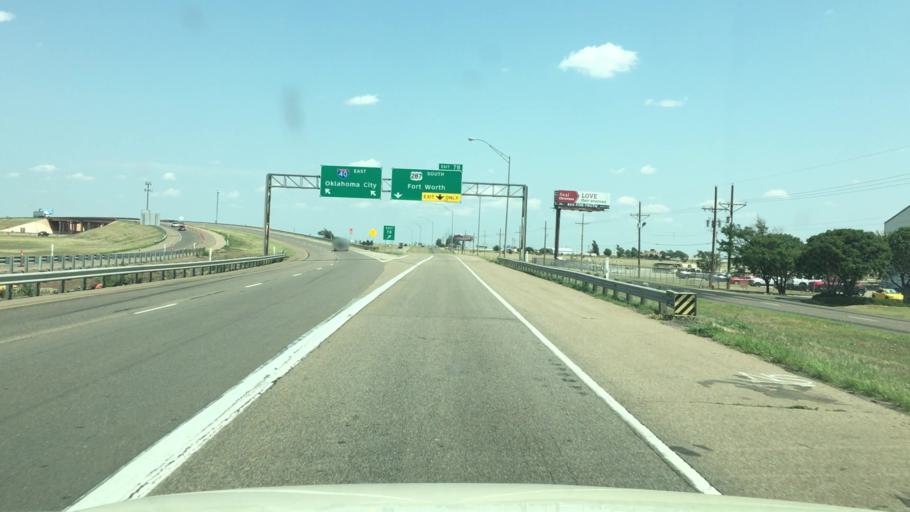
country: US
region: Texas
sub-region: Potter County
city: Amarillo
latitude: 35.1926
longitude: -101.6976
